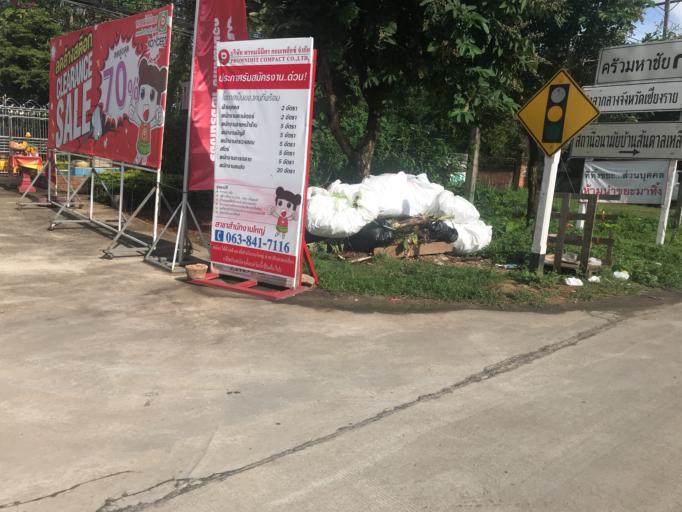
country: TH
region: Chiang Rai
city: Chiang Rai
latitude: 19.9403
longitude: 99.8456
